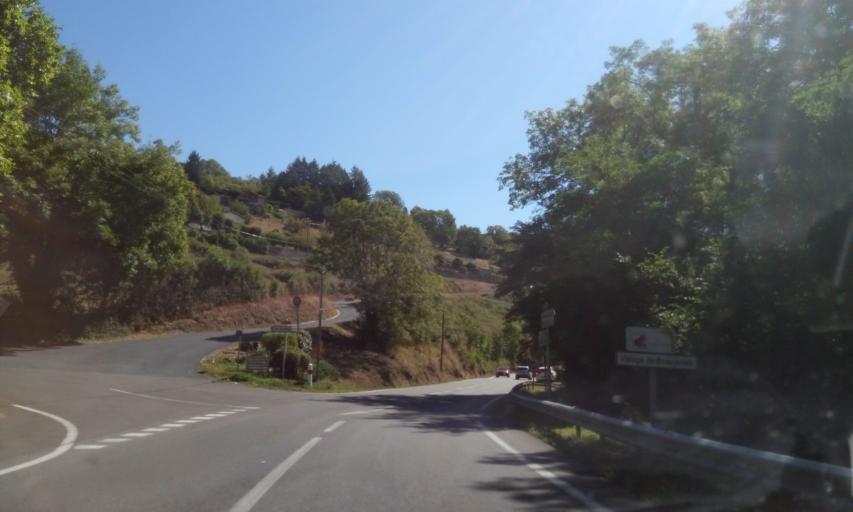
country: FR
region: Rhone-Alpes
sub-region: Departement du Rhone
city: Grandris
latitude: 45.9860
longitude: 4.5069
